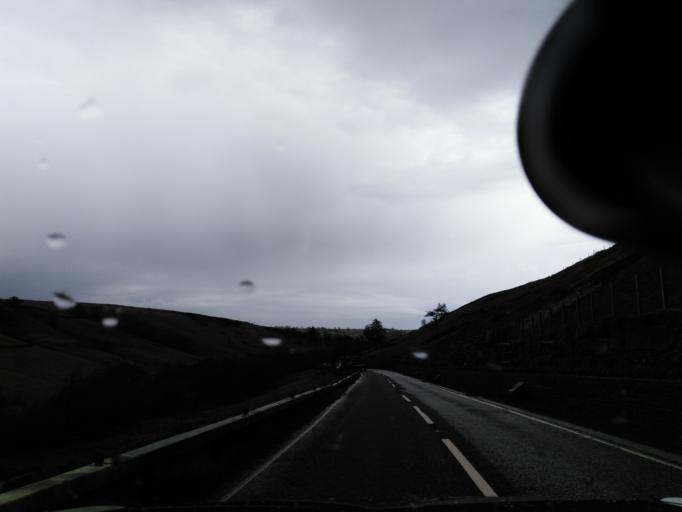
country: GB
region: England
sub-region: Bradford
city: Ilkley
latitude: 53.9939
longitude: -1.7808
